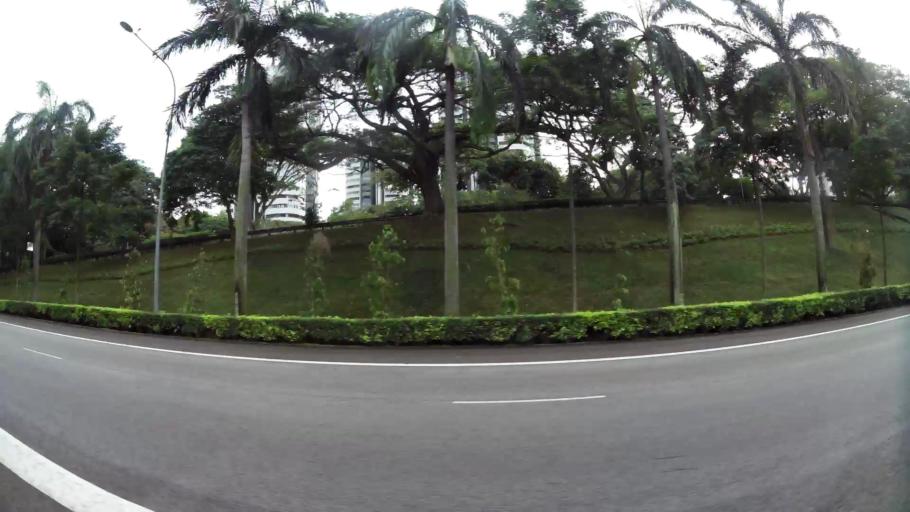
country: SG
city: Singapore
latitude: 1.2781
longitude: 103.8245
